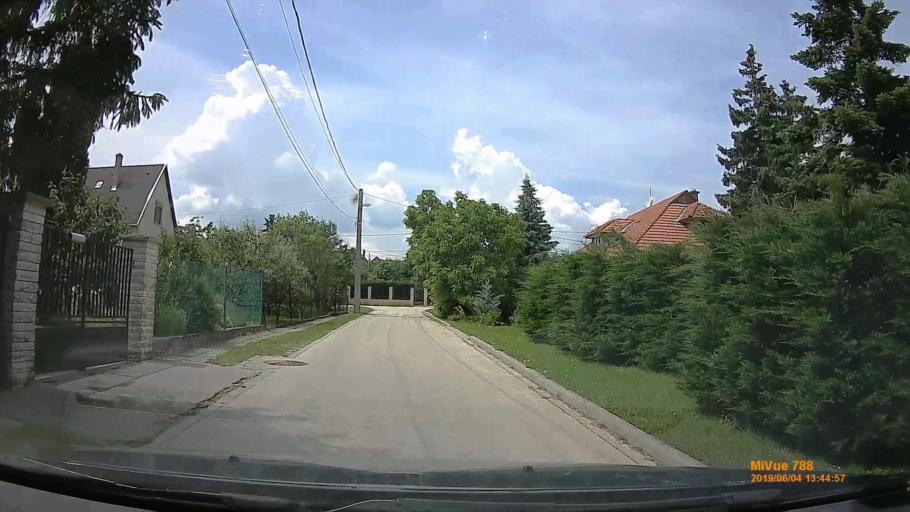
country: HU
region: Budapest
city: Budapest XXII. keruelet
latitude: 47.4300
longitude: 19.0001
